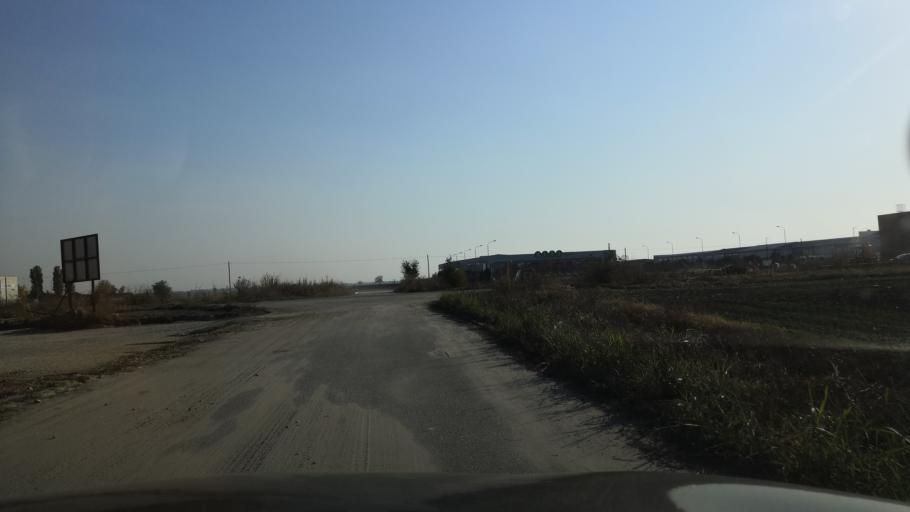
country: RS
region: Autonomna Pokrajina Vojvodina
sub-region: Sremski Okrug
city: Stara Pazova
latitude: 44.9880
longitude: 20.1979
